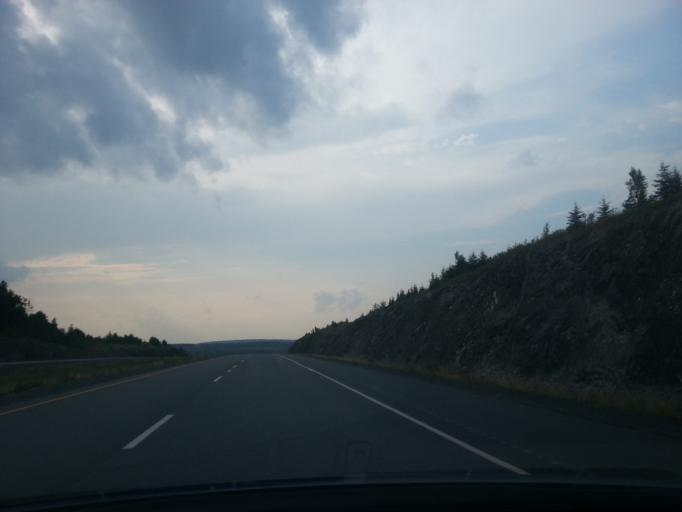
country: CA
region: New Brunswick
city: Harrison Brook
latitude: 47.2217
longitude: -67.9454
